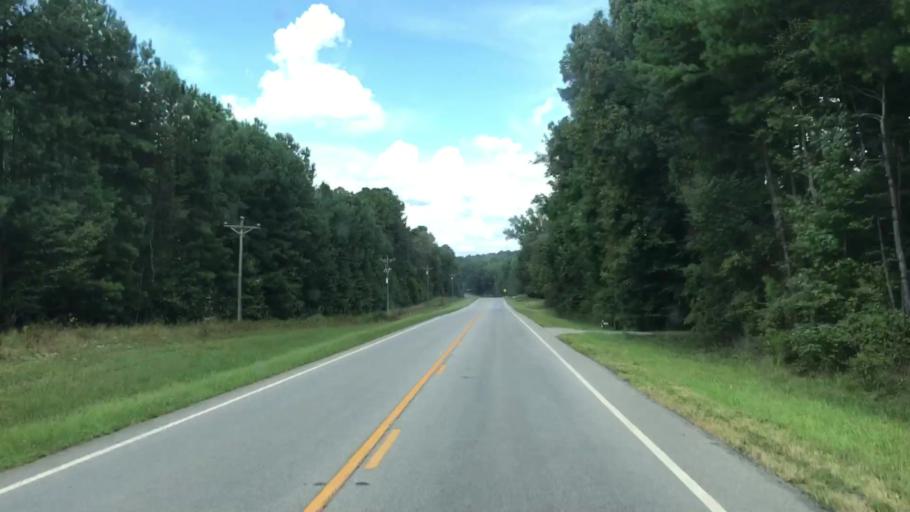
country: US
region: Georgia
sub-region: Greene County
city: Greensboro
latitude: 33.6298
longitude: -83.2154
